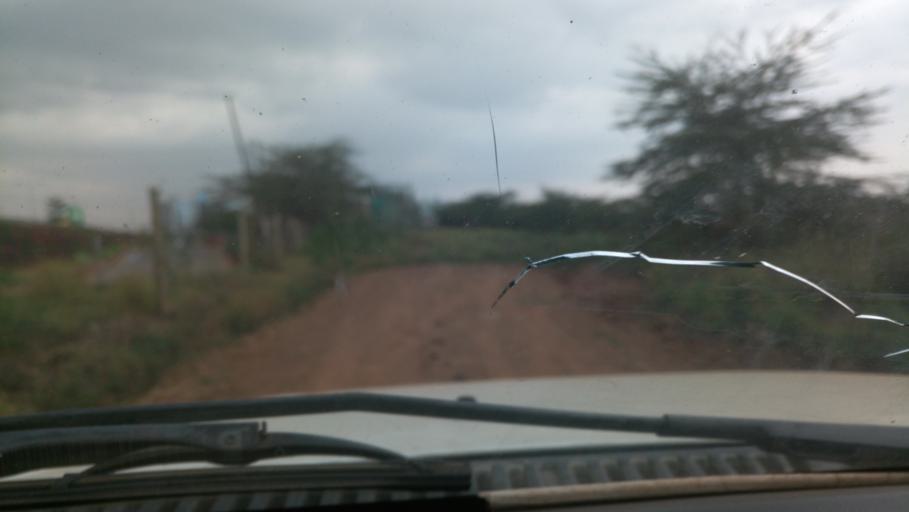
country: KE
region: Nairobi Area
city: Pumwani
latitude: -1.3279
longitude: 36.8435
